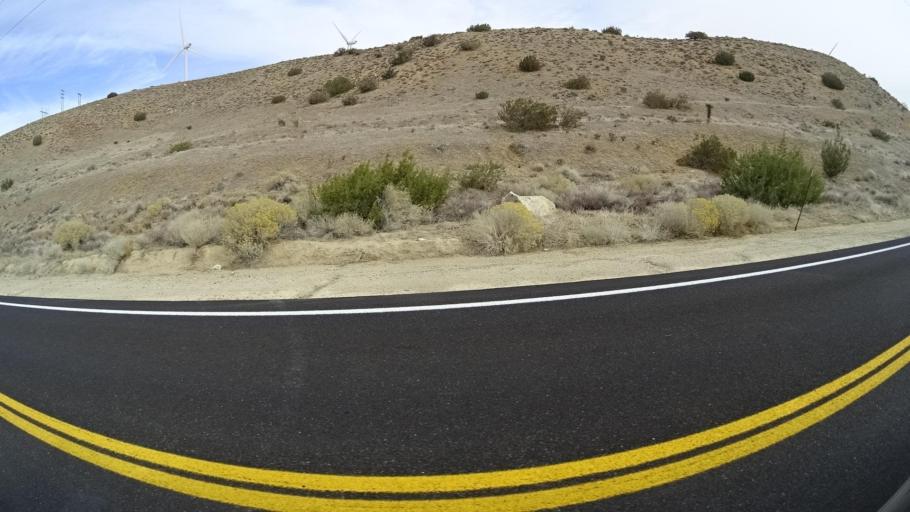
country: US
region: California
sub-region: Kern County
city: Tehachapi
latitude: 35.0504
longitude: -118.3277
